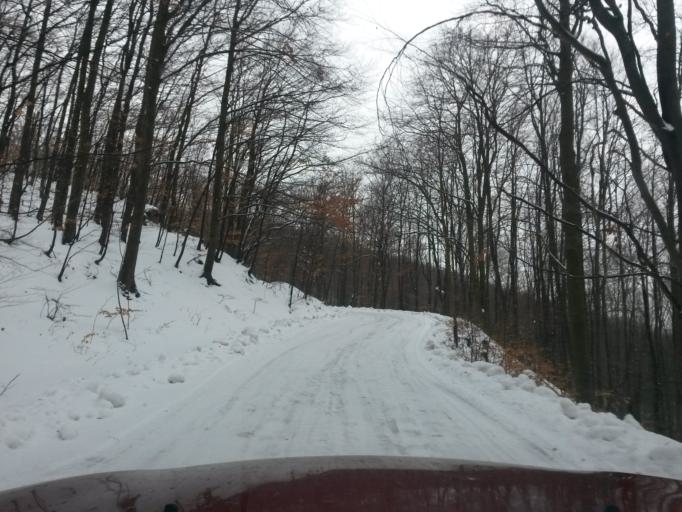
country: SK
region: Kosicky
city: Secovce
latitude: 48.8127
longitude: 21.5179
